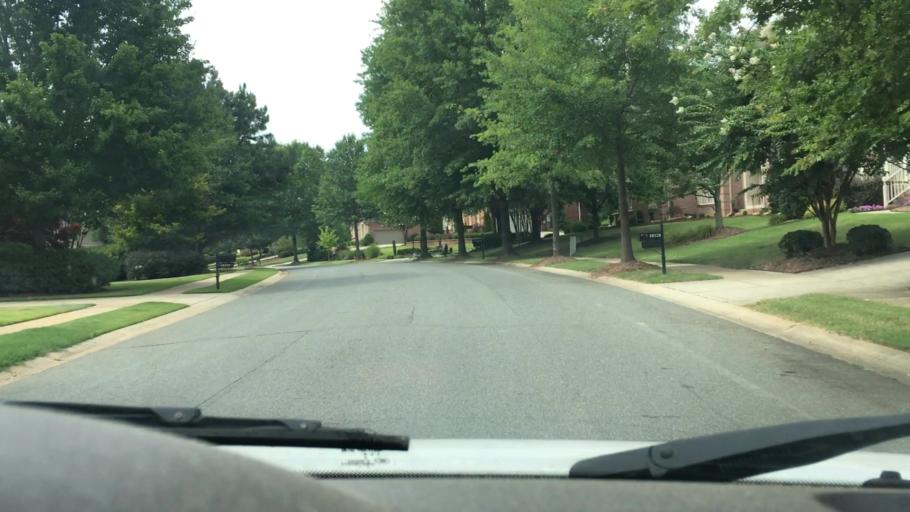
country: US
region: North Carolina
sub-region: Gaston County
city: Davidson
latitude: 35.4674
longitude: -80.7830
